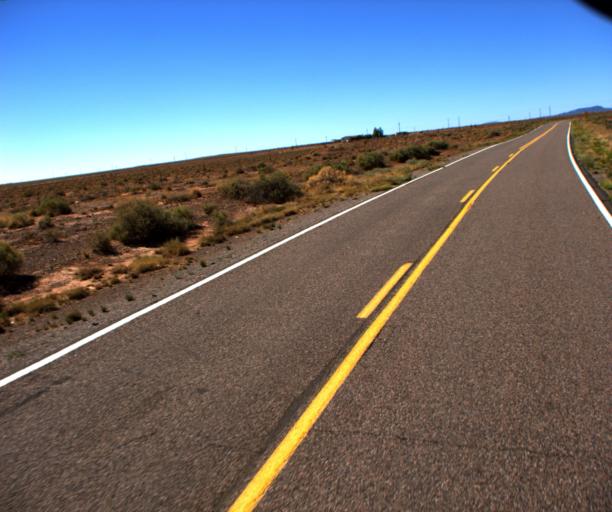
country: US
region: Arizona
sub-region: Coconino County
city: LeChee
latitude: 35.0908
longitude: -110.8605
